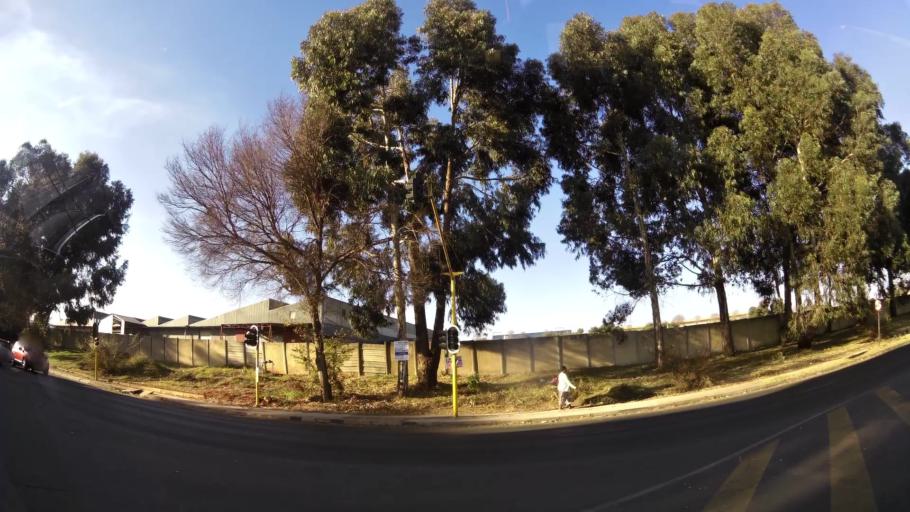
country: ZA
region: Gauteng
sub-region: City of Johannesburg Metropolitan Municipality
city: Roodepoort
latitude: -26.1417
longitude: 27.8581
